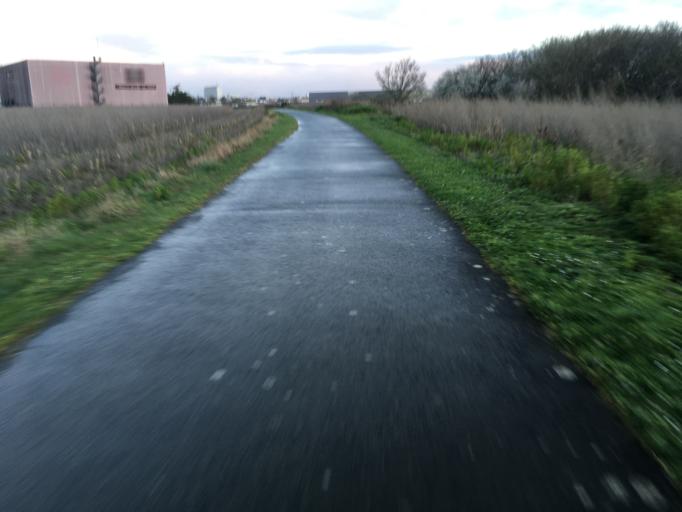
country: FR
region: Poitou-Charentes
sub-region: Departement de la Charente-Maritime
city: Nieul-sur-Mer
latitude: 46.1764
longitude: -1.2096
